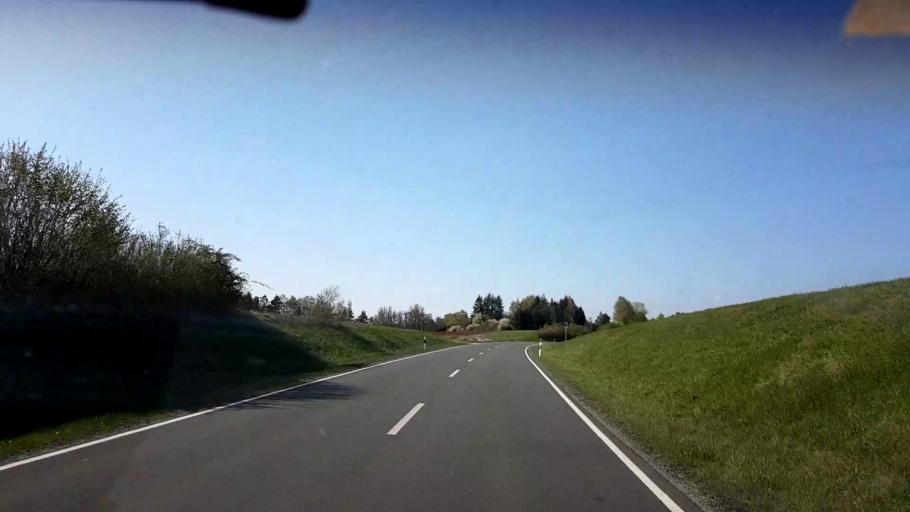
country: DE
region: Bavaria
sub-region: Upper Franconia
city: Hollfeld
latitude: 49.9214
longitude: 11.3069
